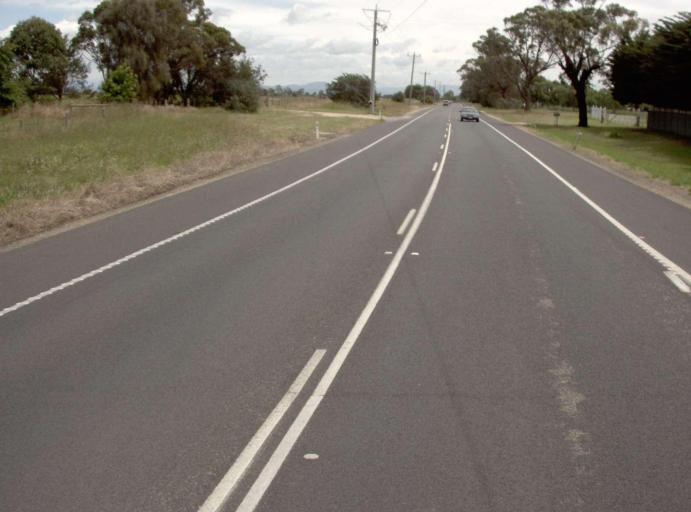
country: AU
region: Victoria
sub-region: Wellington
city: Sale
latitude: -38.0616
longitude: 147.0287
